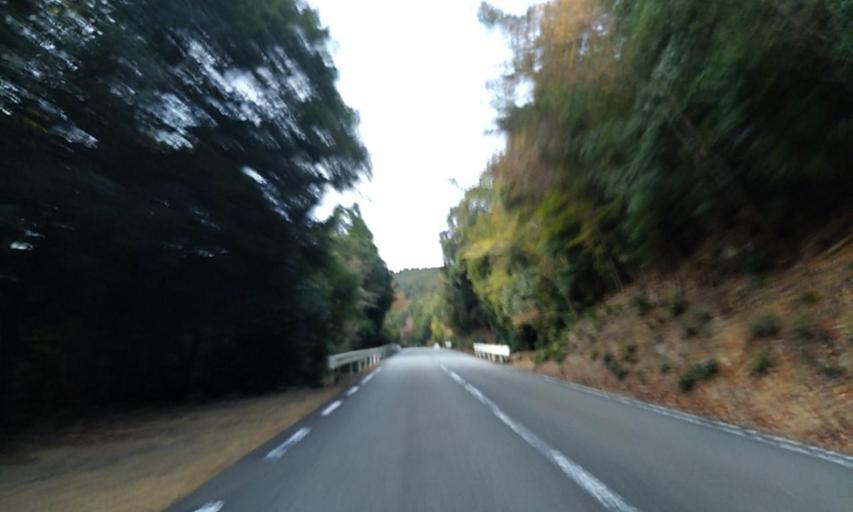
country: JP
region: Mie
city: Toba
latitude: 34.4565
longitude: 136.7814
